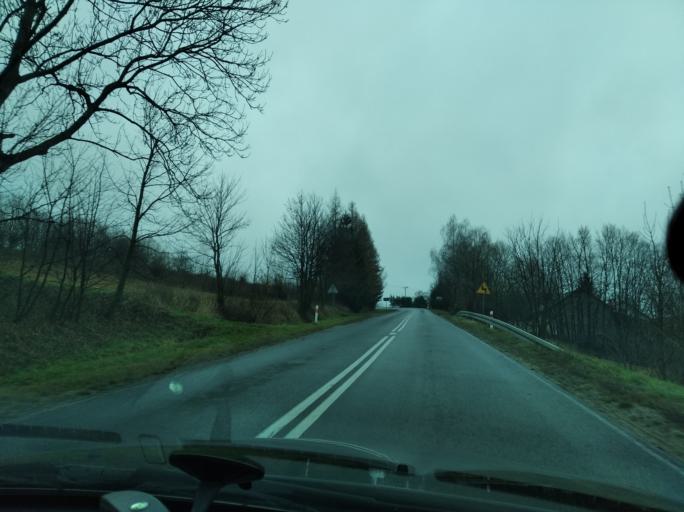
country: PL
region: Subcarpathian Voivodeship
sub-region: Powiat przeworski
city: Jawornik Polski
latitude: 49.8847
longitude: 22.2397
